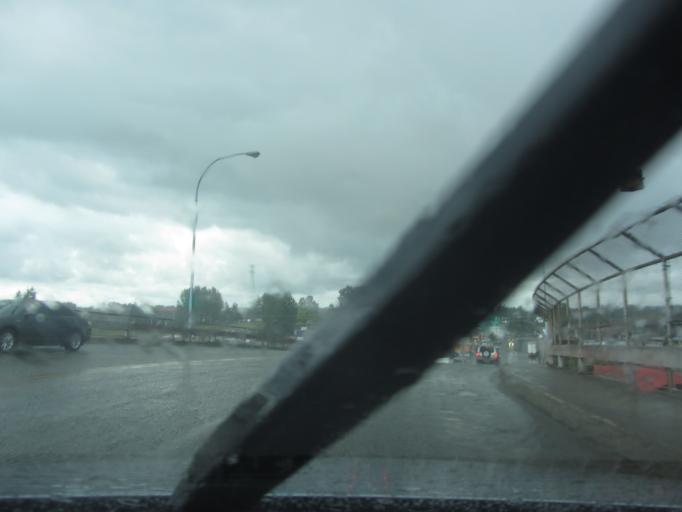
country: CA
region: British Columbia
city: Abbotsford
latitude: 49.1336
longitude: -122.3002
